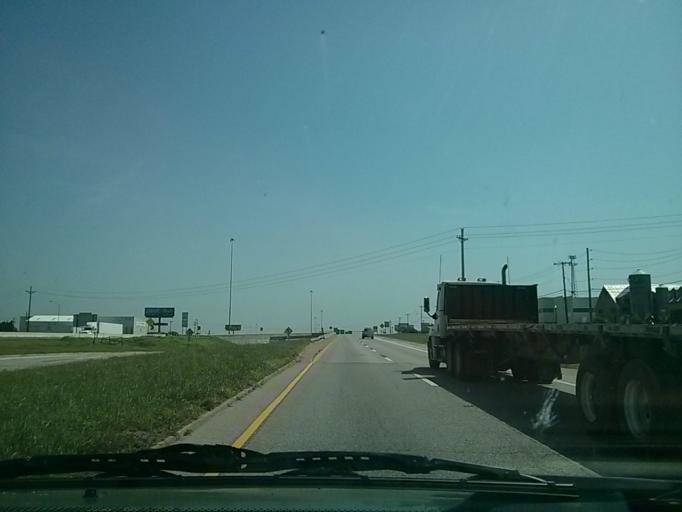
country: US
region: Oklahoma
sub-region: Tulsa County
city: Oakhurst
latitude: 36.0725
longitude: -96.0576
